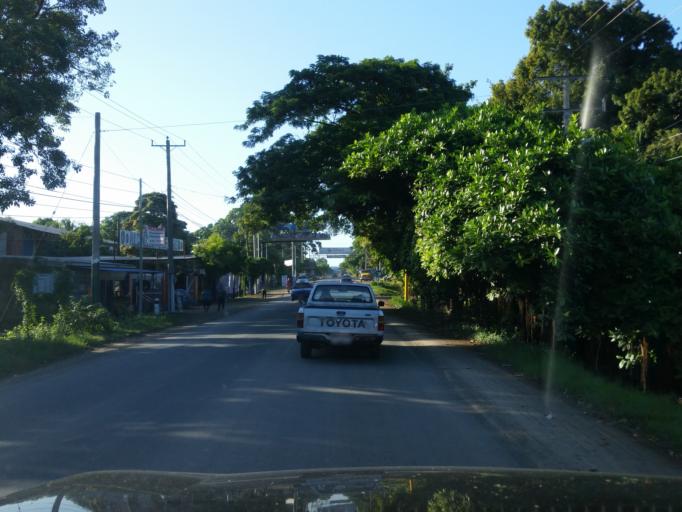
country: NI
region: Rivas
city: Rivas
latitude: 11.4463
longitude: -85.8293
